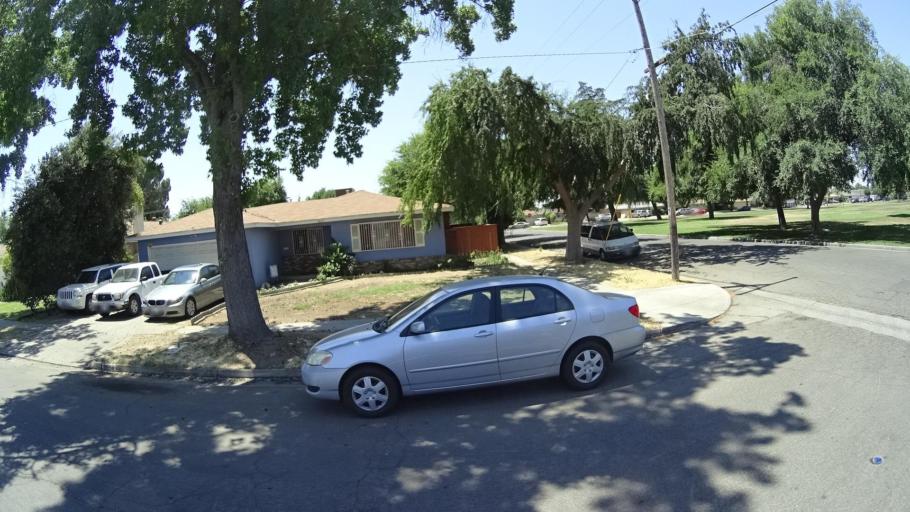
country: US
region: California
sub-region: Fresno County
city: Fresno
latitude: 36.7989
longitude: -119.7608
